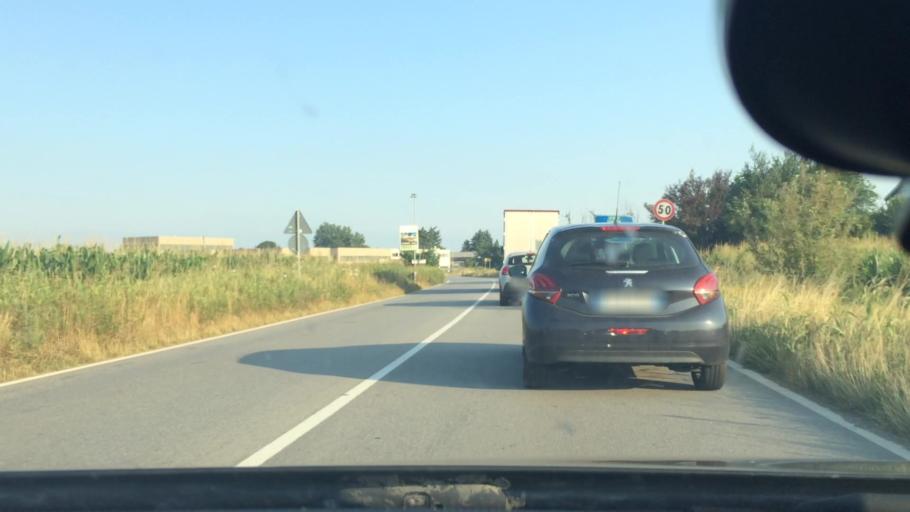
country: IT
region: Lombardy
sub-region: Citta metropolitana di Milano
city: Mantegazza
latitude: 45.5099
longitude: 8.9623
